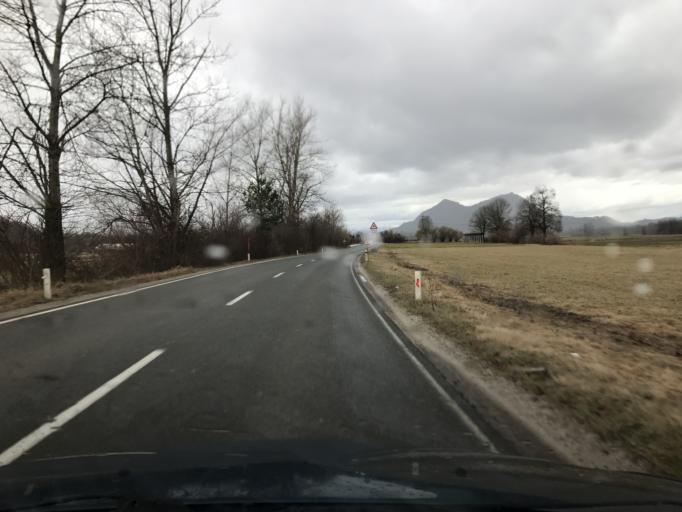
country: SI
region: Ljubljana
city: Ljubljana
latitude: 46.0994
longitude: 14.5125
